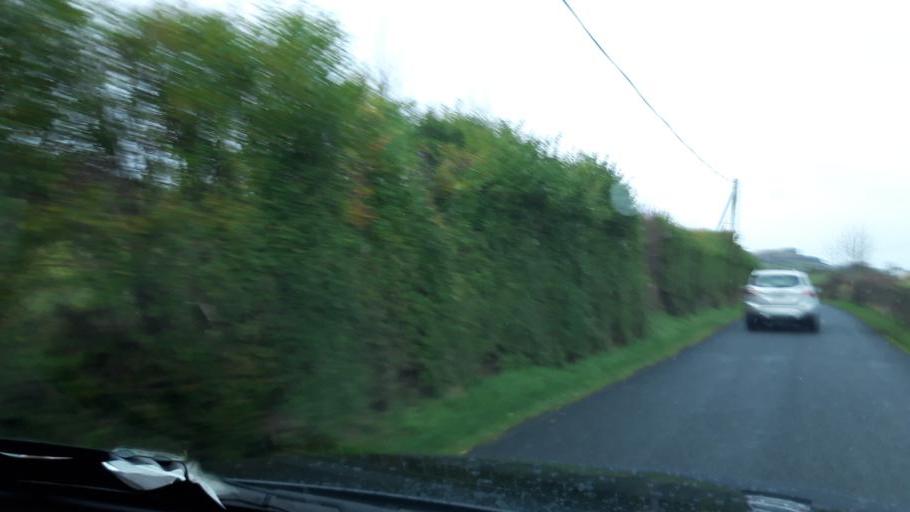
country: IE
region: Ulster
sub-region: County Donegal
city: Buncrana
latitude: 55.2384
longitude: -7.6190
